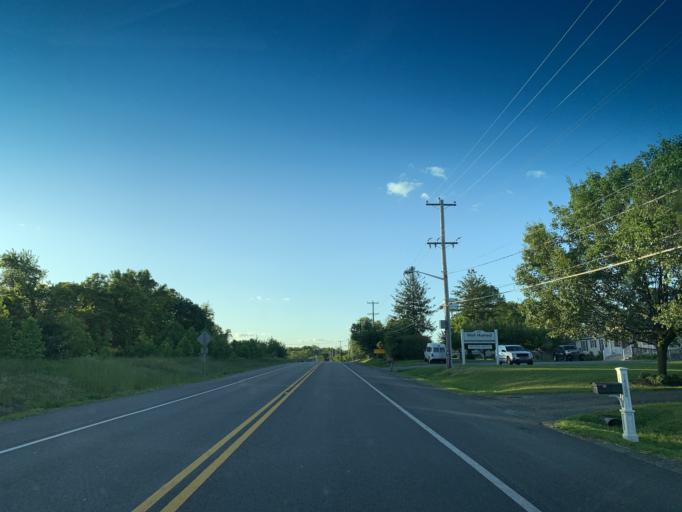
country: US
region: Maryland
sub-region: Cecil County
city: Elkton
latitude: 39.6513
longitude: -75.8496
